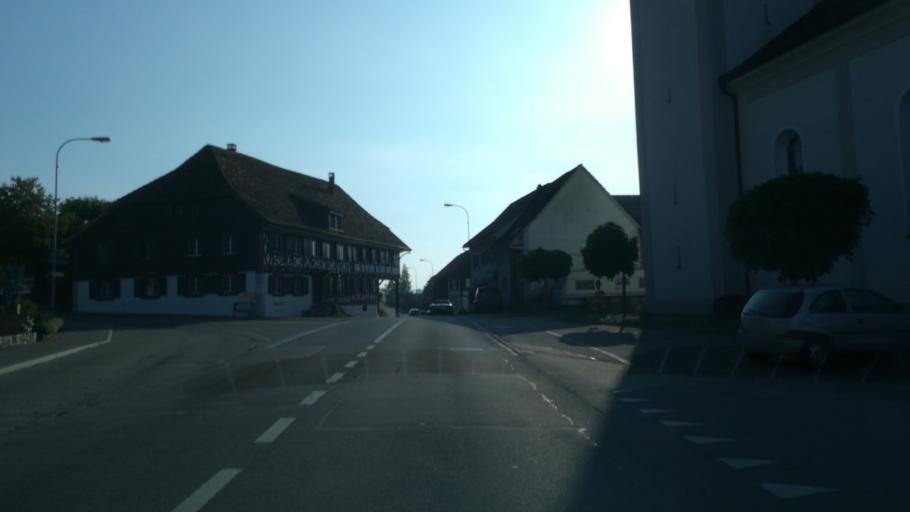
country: CH
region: Thurgau
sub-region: Frauenfeld District
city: Huttwilen
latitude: 47.6048
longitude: 8.9097
